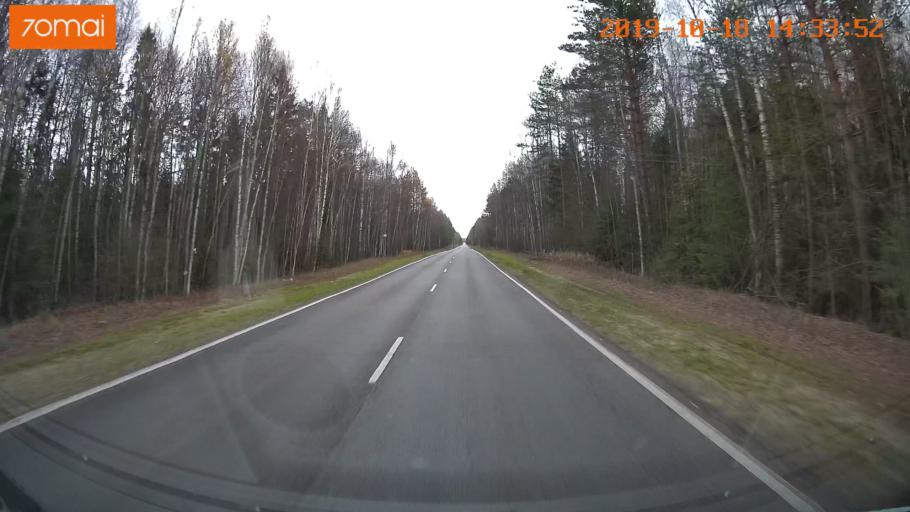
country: RU
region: Vladimir
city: Velikodvorskiy
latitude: 55.2061
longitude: 40.6050
